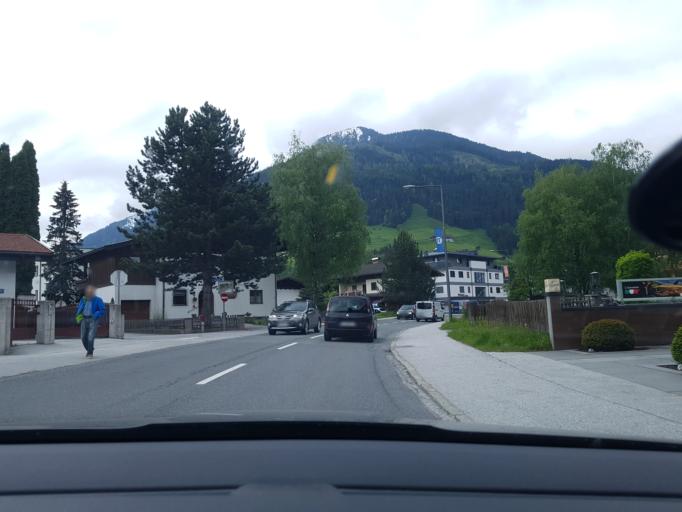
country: AT
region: Salzburg
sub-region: Politischer Bezirk Zell am See
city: Mittersill
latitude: 47.2794
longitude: 12.4795
